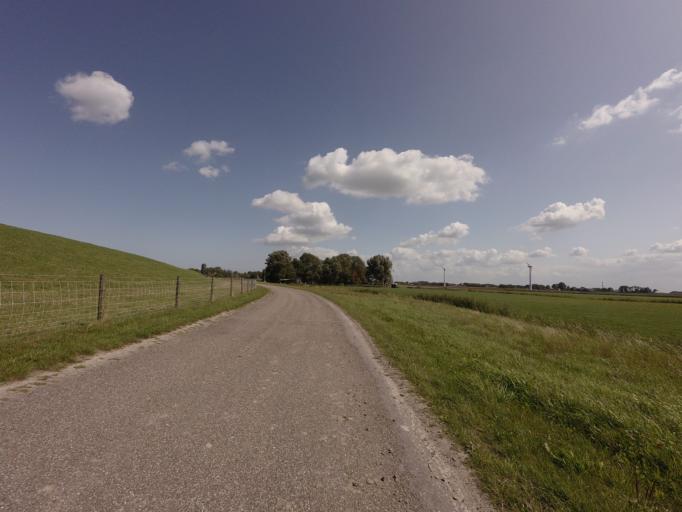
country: NL
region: Friesland
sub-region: Gemeente Ferwerderadiel
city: Hallum
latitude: 53.3250
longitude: 5.7664
